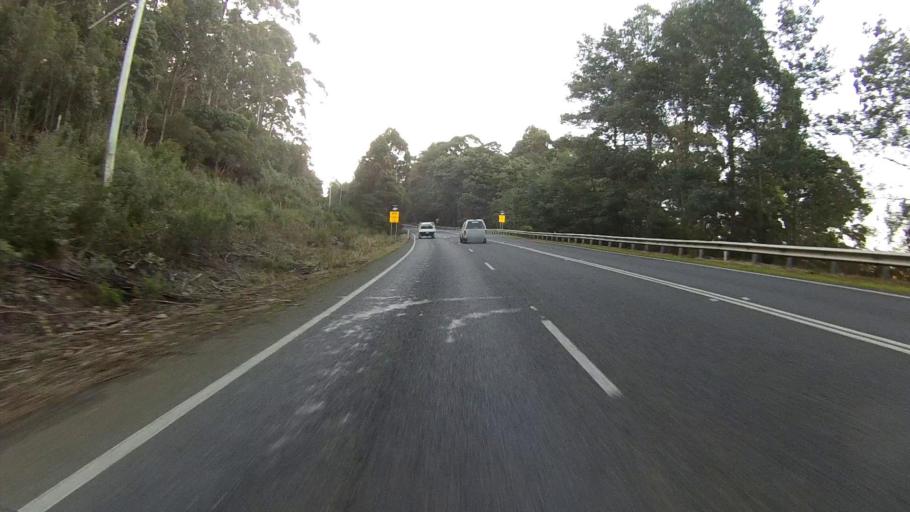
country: AU
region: Tasmania
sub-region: Sorell
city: Sorell
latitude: -43.0110
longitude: 147.9261
